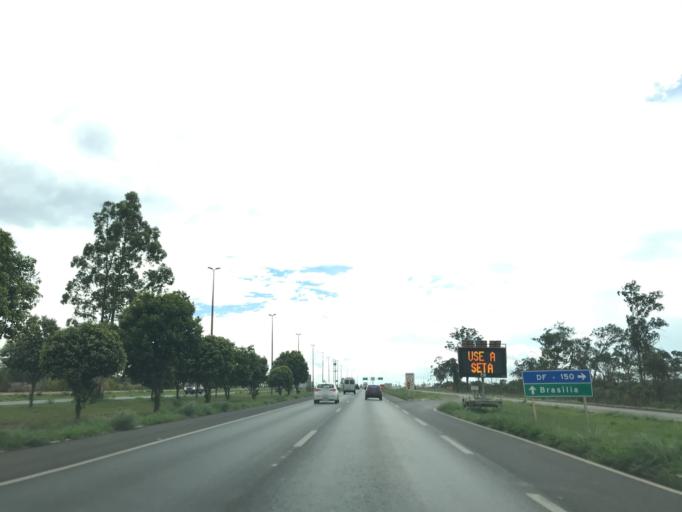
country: BR
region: Federal District
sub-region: Brasilia
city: Brasilia
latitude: -15.6859
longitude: -47.8510
